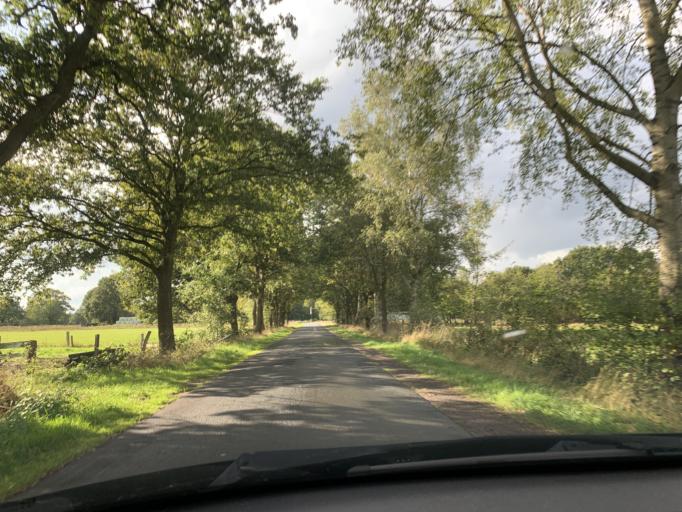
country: DE
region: Lower Saxony
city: Westerstede
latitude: 53.3112
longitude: 7.9792
